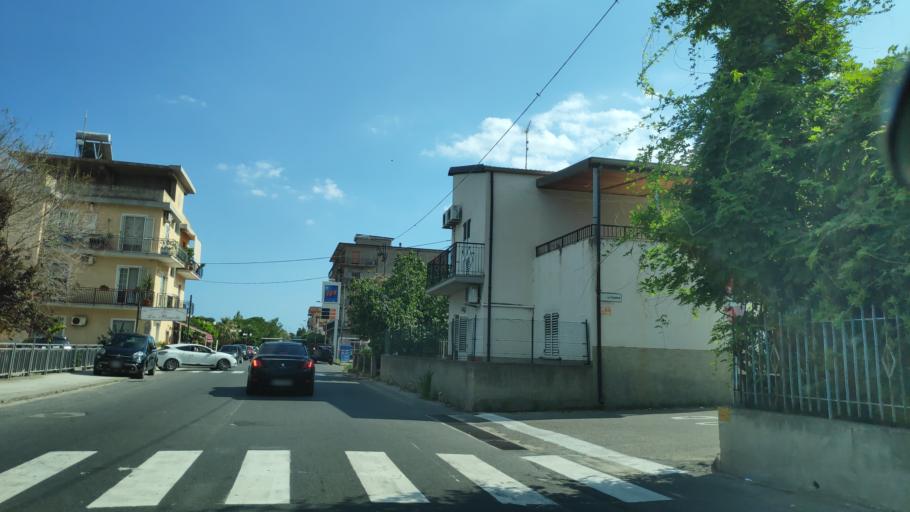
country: IT
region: Calabria
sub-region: Provincia di Catanzaro
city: Santa Caterina dello Ionio Marina
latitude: 38.5335
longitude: 16.5703
